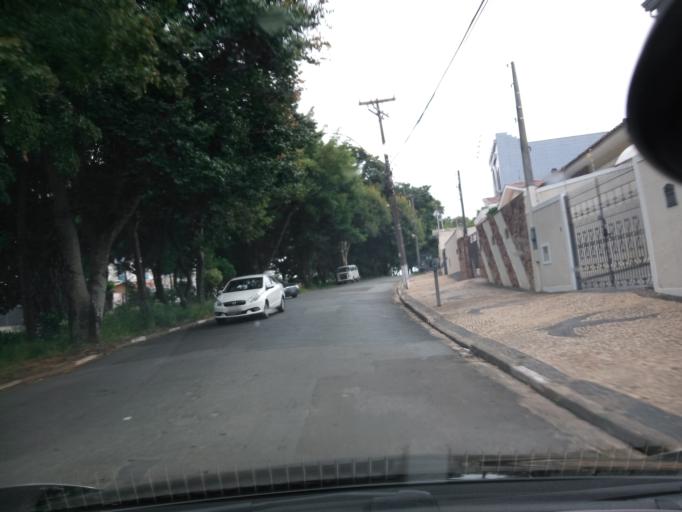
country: BR
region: Sao Paulo
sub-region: Campinas
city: Campinas
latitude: -22.8785
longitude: -47.0381
